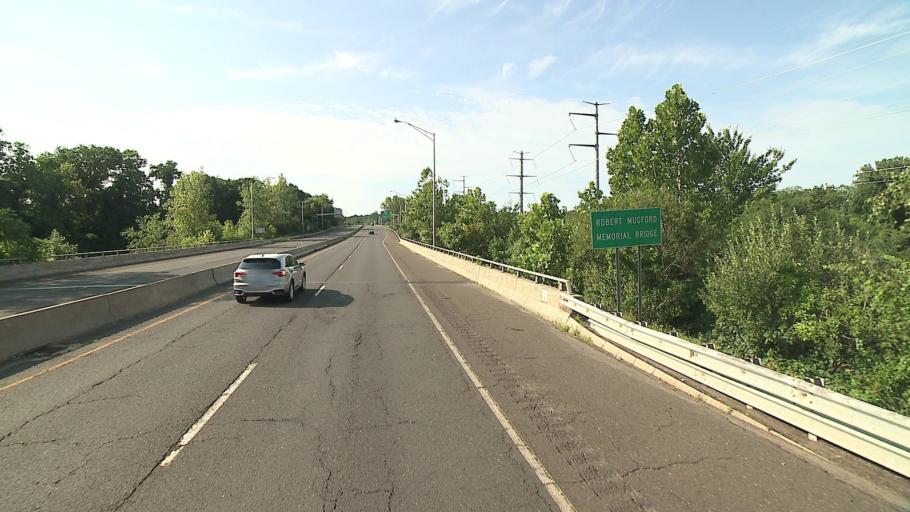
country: US
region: Connecticut
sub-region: Fairfield County
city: Norwalk
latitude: 41.1344
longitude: -73.4294
